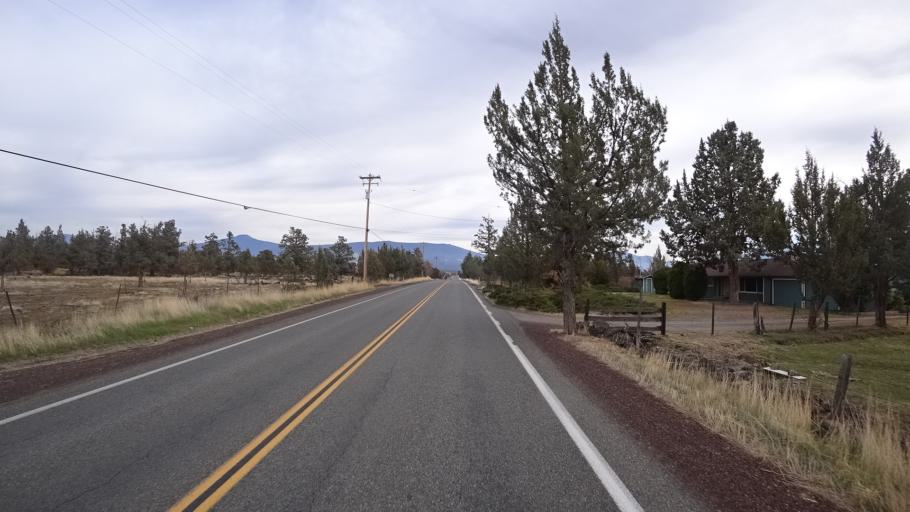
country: US
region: California
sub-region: Siskiyou County
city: Montague
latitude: 41.6240
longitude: -122.4219
